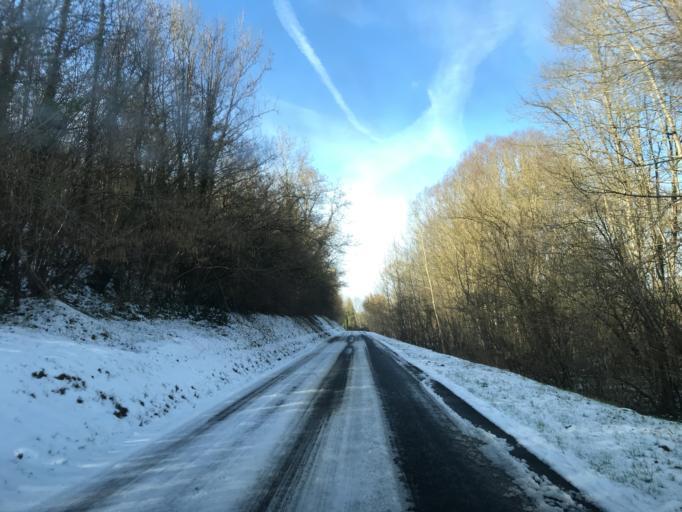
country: FR
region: Haute-Normandie
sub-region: Departement de l'Eure
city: Saint-Aubin-sur-Gaillon
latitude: 49.0797
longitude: 1.2803
